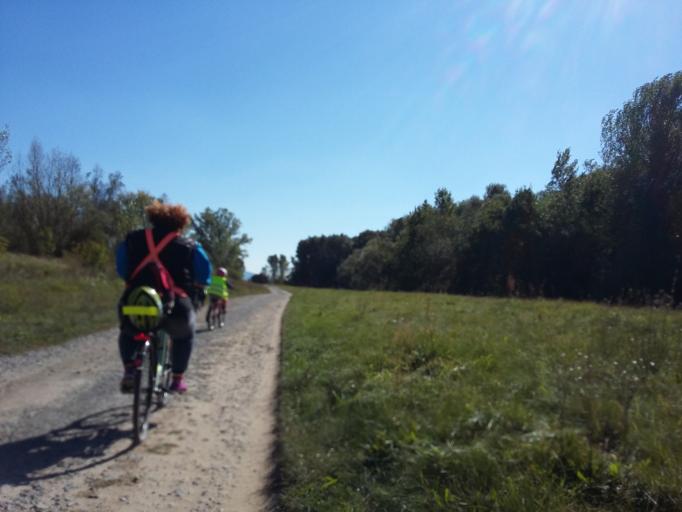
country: AT
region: Lower Austria
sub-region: Politischer Bezirk Ganserndorf
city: Marchegg
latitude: 48.3181
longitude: 16.9113
